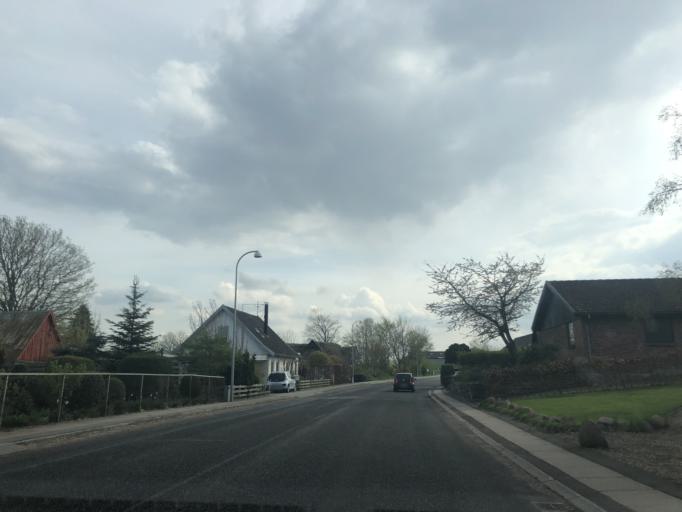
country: DK
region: Zealand
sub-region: Roskilde Kommune
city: Gundsomagle
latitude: 55.6946
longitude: 12.1349
